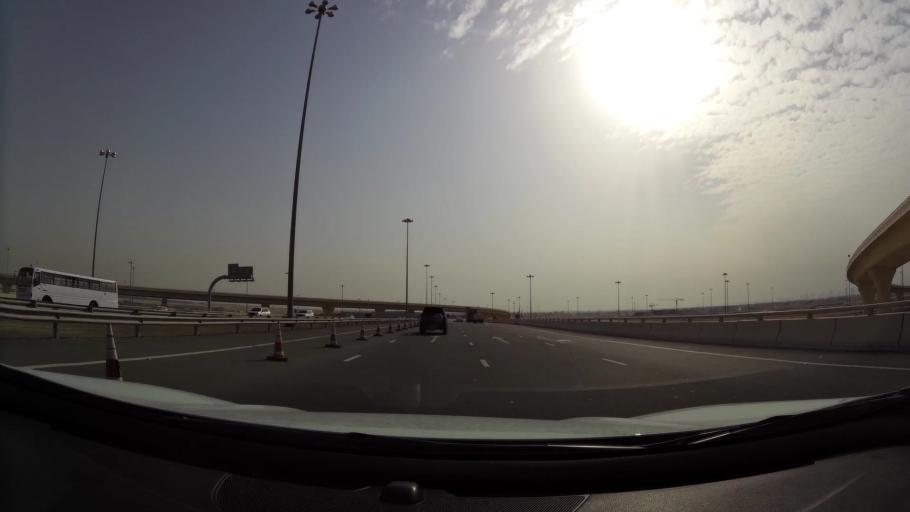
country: AE
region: Abu Dhabi
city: Abu Dhabi
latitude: 24.3104
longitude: 54.6020
